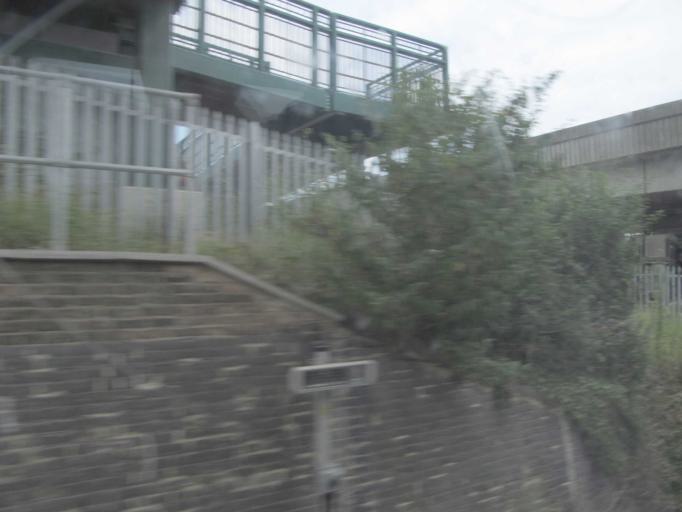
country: GB
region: England
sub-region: Greater London
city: West Drayton
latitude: 51.5079
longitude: -0.4514
